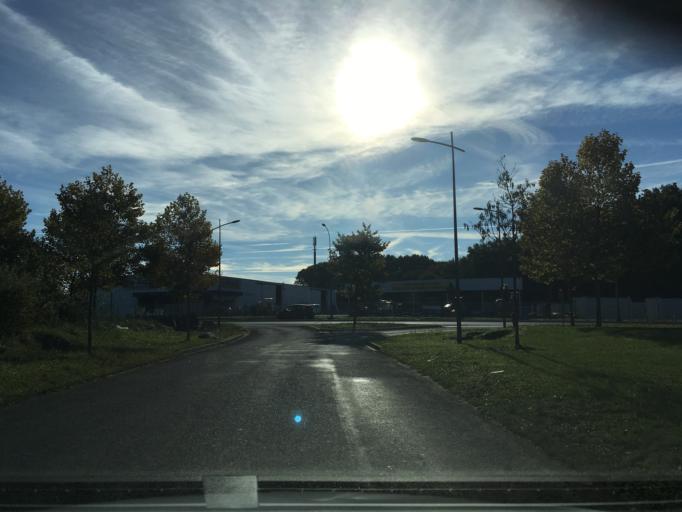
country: FR
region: Aquitaine
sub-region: Departement des Pyrenees-Atlantiques
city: Buros
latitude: 43.3201
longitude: -0.3064
